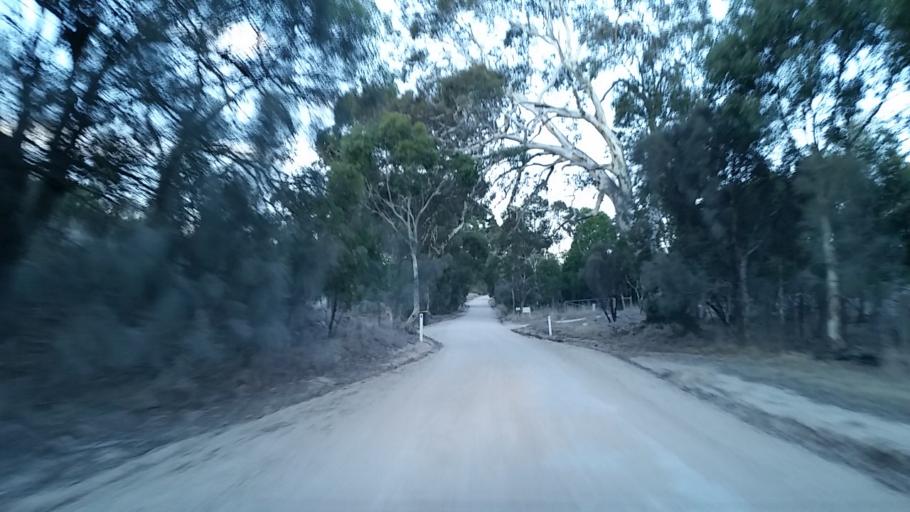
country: AU
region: South Australia
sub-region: Mount Barker
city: Nairne
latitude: -35.0946
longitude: 138.9587
